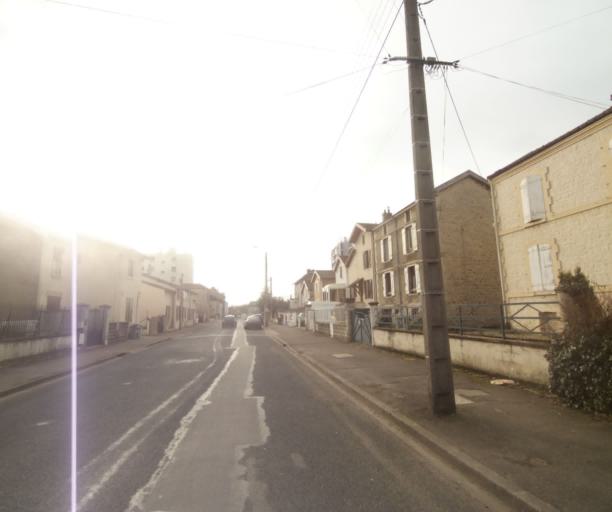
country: FR
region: Champagne-Ardenne
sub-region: Departement de la Haute-Marne
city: Saint-Dizier
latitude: 48.6396
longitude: 4.9335
